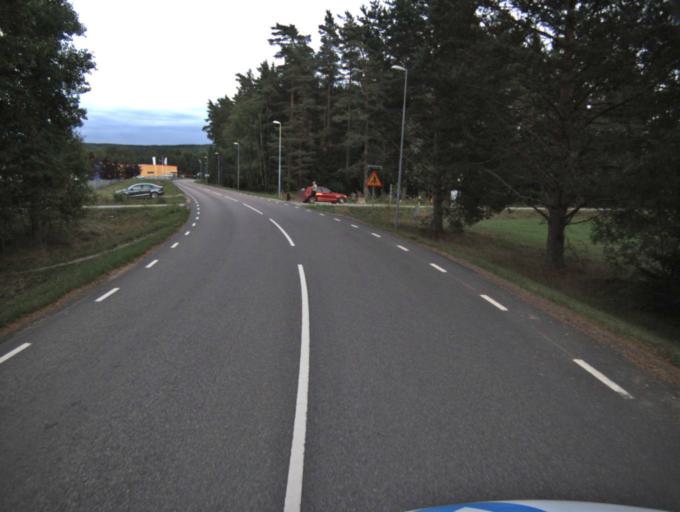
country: SE
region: Vaestra Goetaland
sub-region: Ulricehamns Kommun
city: Ulricehamn
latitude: 57.8250
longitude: 13.4169
